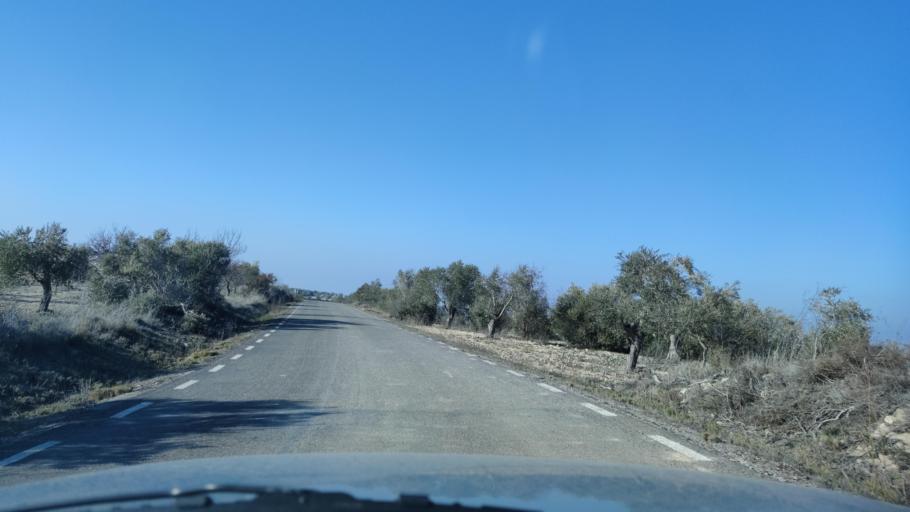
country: ES
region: Catalonia
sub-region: Provincia de Lleida
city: Torrebesses
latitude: 41.4378
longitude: 0.5635
